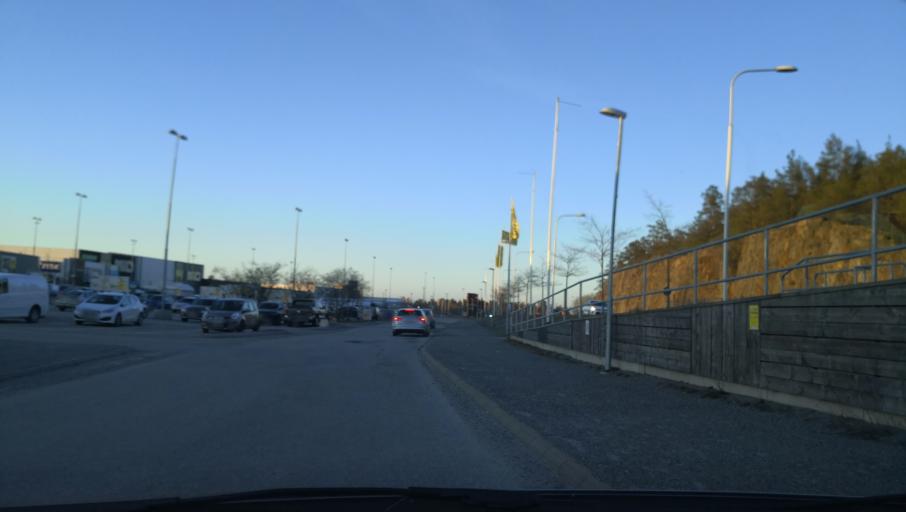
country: SE
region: Stockholm
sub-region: Varmdo Kommun
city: Gustavsberg
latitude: 59.3090
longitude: 18.3848
